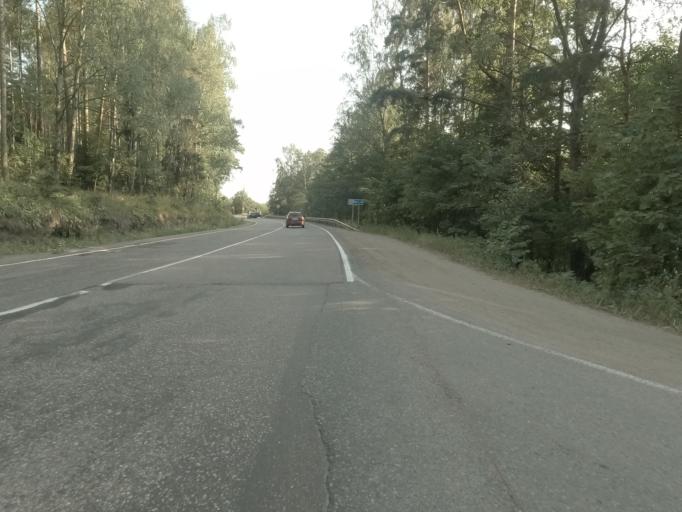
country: RU
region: Leningrad
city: Vyborg
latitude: 60.7379
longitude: 28.7589
